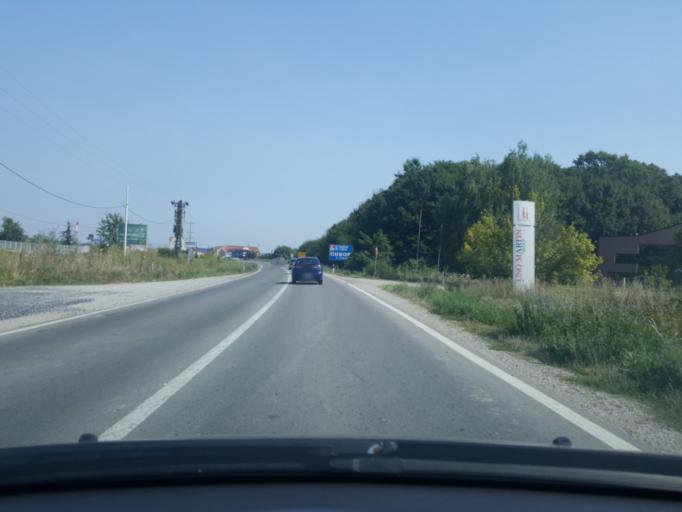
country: RS
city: Majur
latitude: 44.7579
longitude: 19.6471
